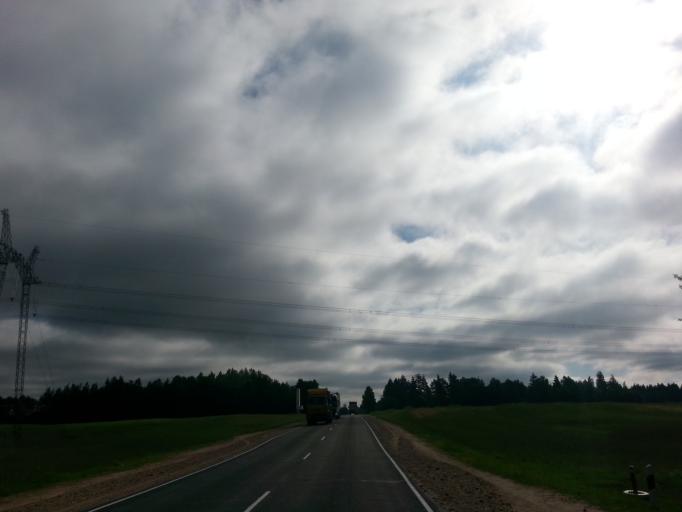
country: BY
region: Vitebsk
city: Mosar
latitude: 55.0801
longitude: 27.4443
